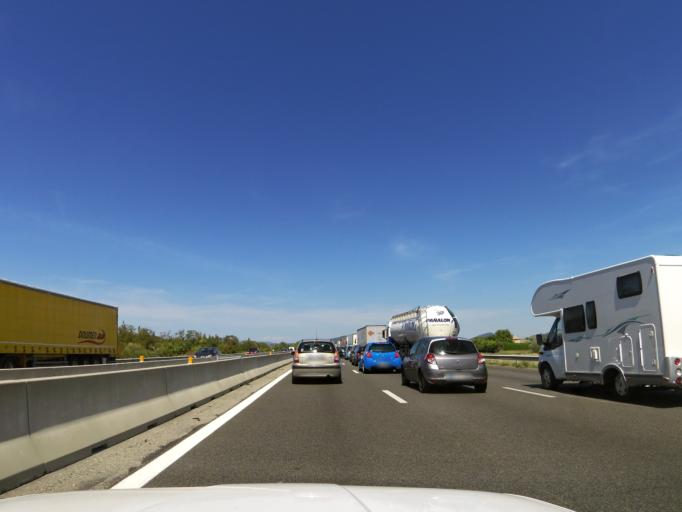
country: FR
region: Rhone-Alpes
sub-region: Departement de la Drome
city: La Garde-Adhemar
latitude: 44.3916
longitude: 4.7304
